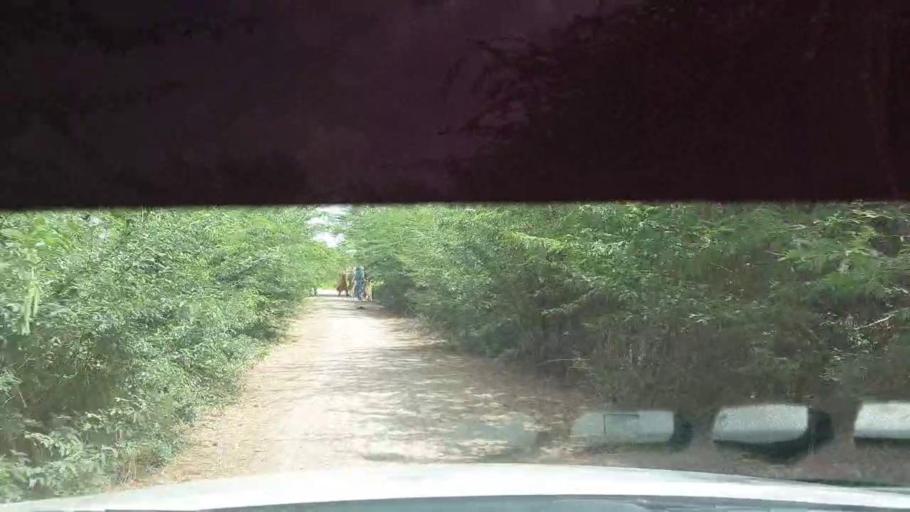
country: PK
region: Sindh
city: Kadhan
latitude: 24.6142
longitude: 69.0259
